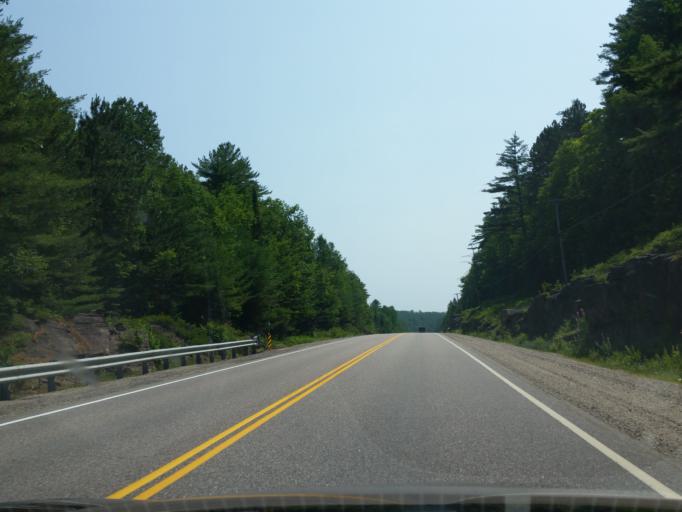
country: CA
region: Ontario
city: Deep River
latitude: 46.1827
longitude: -77.7442
